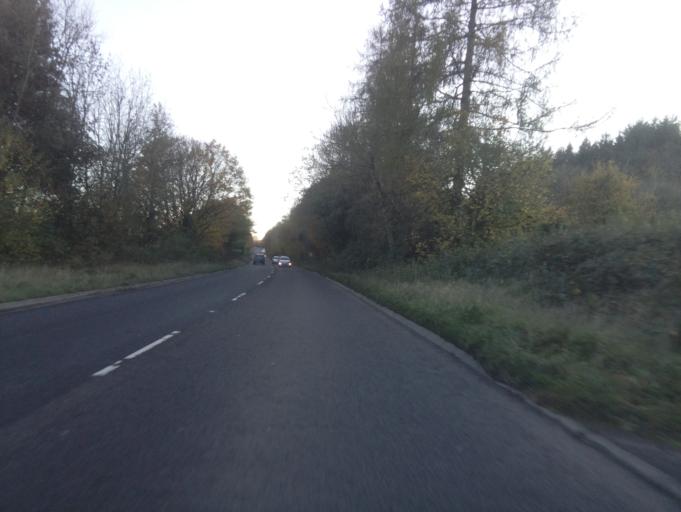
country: GB
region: England
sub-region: Wiltshire
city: Warminster
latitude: 51.1792
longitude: -2.1948
